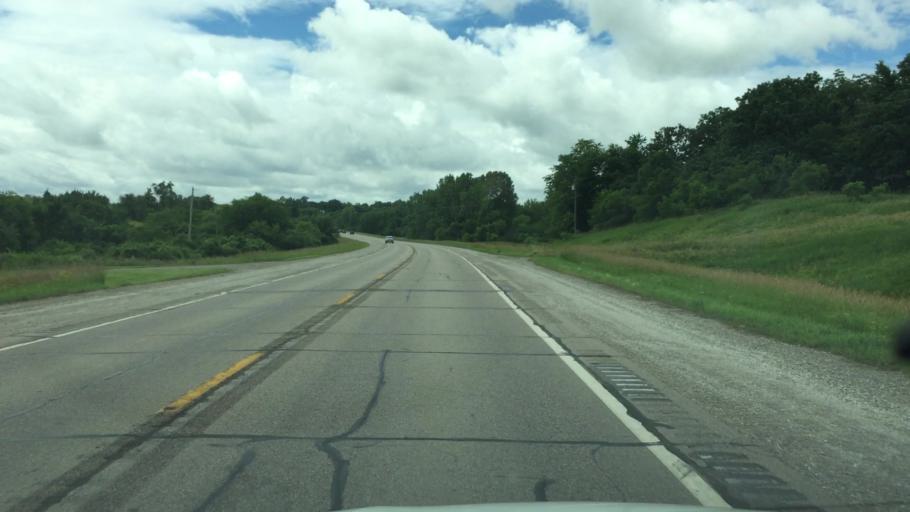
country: US
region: Iowa
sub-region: Jasper County
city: Monroe
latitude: 41.5377
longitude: -93.1007
